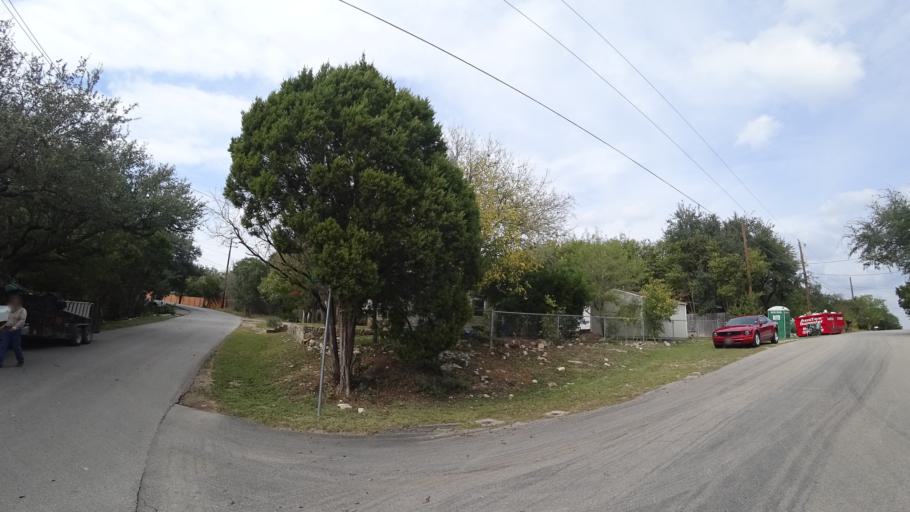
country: US
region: Texas
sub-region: Travis County
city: Hudson Bend
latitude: 30.3736
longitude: -97.9217
